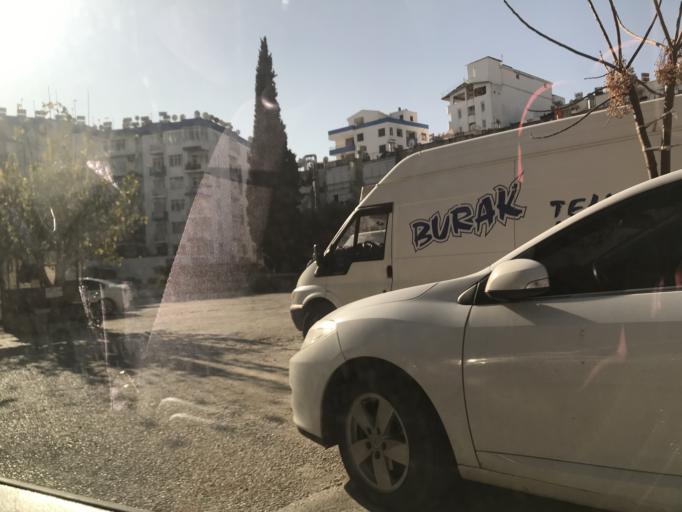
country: TR
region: Antalya
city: Antalya
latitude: 36.8922
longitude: 30.6955
